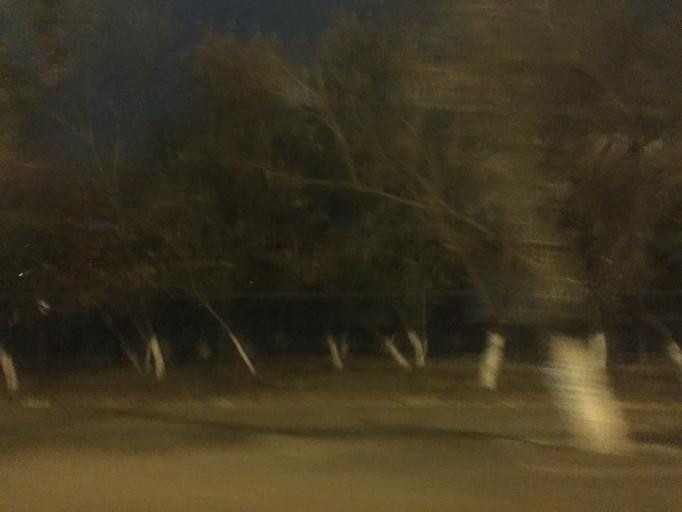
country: KZ
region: Astana Qalasy
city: Astana
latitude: 51.1630
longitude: 71.4176
